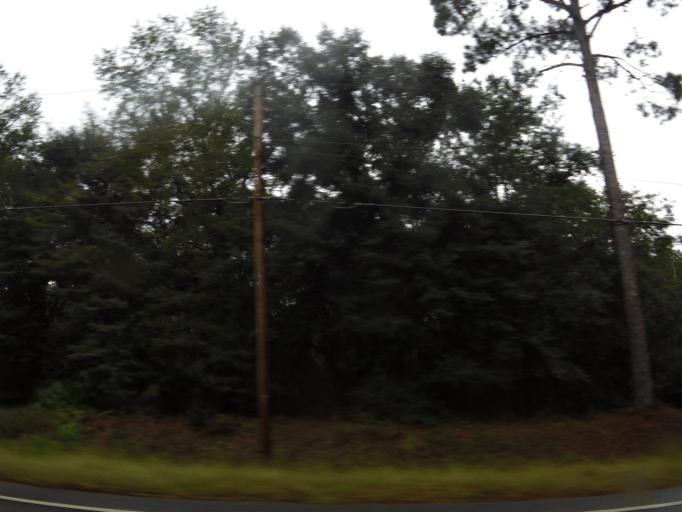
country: US
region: Georgia
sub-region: Wayne County
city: Jesup
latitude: 31.5697
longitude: -81.8863
